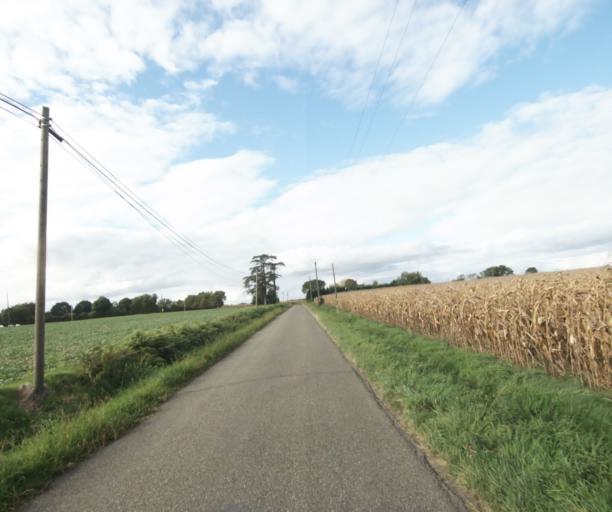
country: FR
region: Midi-Pyrenees
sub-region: Departement du Gers
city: Eauze
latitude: 43.8706
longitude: 0.0913
